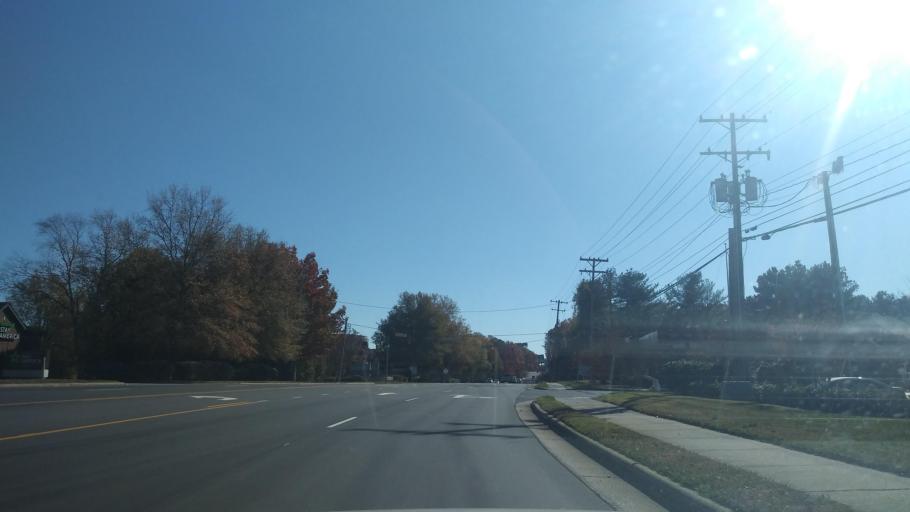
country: US
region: North Carolina
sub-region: Guilford County
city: Jamestown
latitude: 36.0525
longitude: -79.8902
